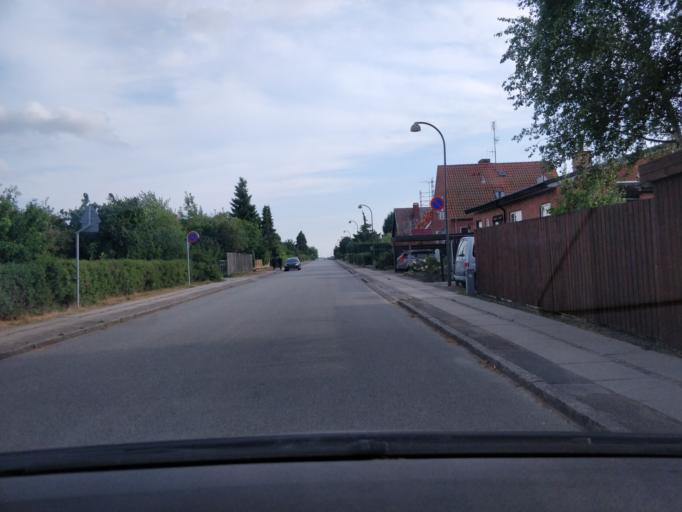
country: DK
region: Capital Region
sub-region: Herlev Kommune
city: Herlev
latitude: 55.7294
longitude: 12.4225
